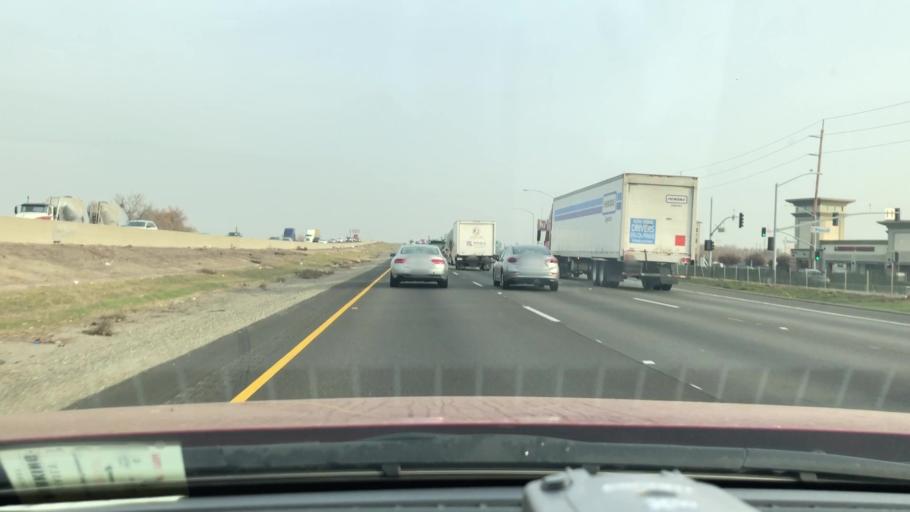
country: US
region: California
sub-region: San Joaquin County
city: Lathrop
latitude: 37.8217
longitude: -121.2918
